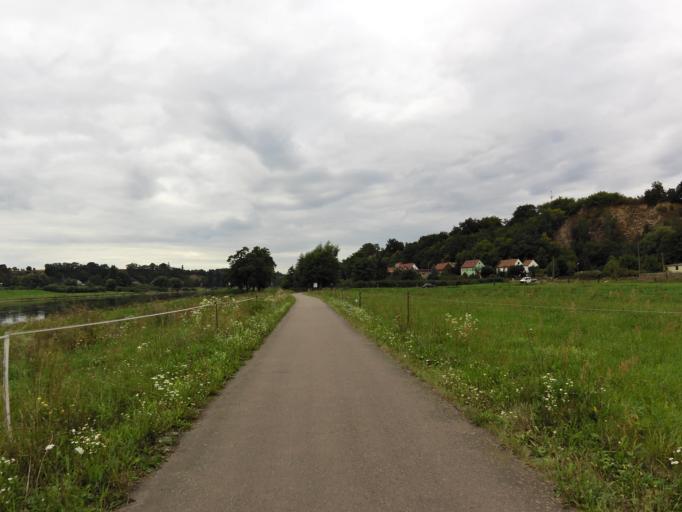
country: DE
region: Saxony
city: Meissen
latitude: 51.1987
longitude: 13.4142
